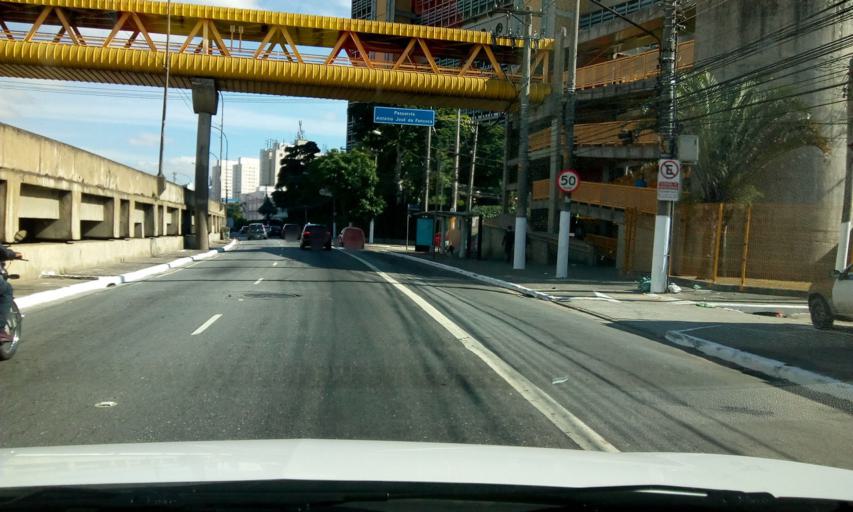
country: BR
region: Sao Paulo
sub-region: Sao Paulo
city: Sao Paulo
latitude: -23.5589
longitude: -46.6145
